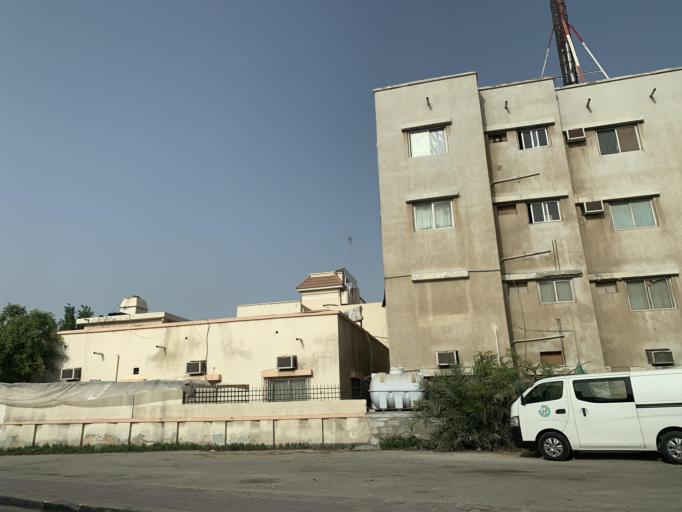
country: BH
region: Manama
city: Manama
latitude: 26.2067
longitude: 50.5892
